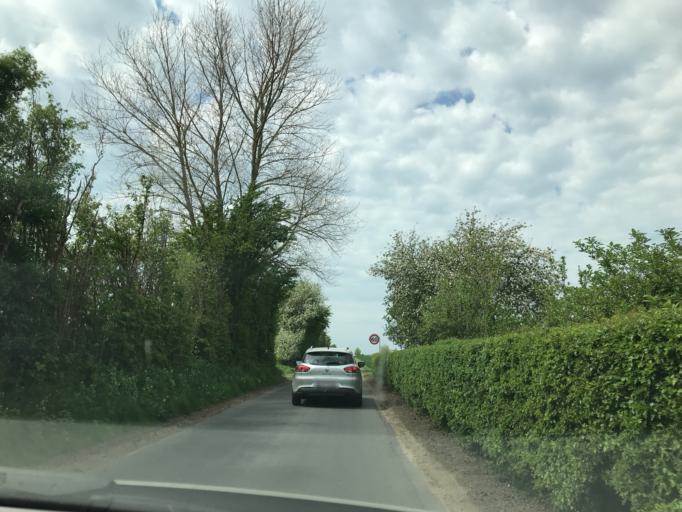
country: DK
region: South Denmark
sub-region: Assens Kommune
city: Assens
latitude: 55.3337
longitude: 9.8955
